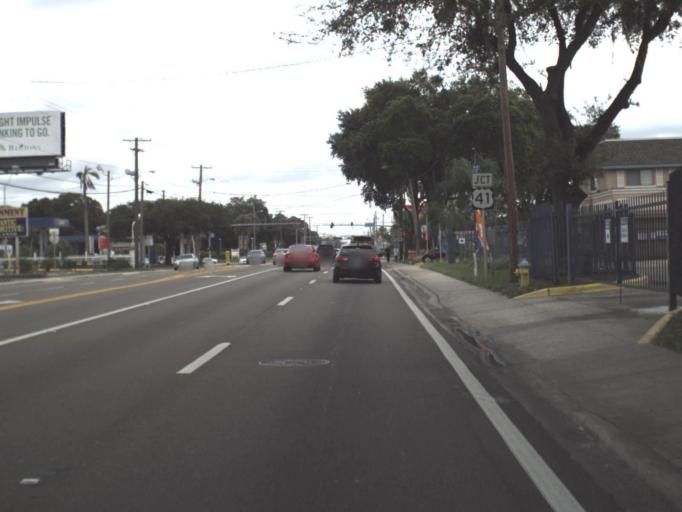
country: US
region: Florida
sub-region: Hillsborough County
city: University
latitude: 28.0692
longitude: -82.4528
